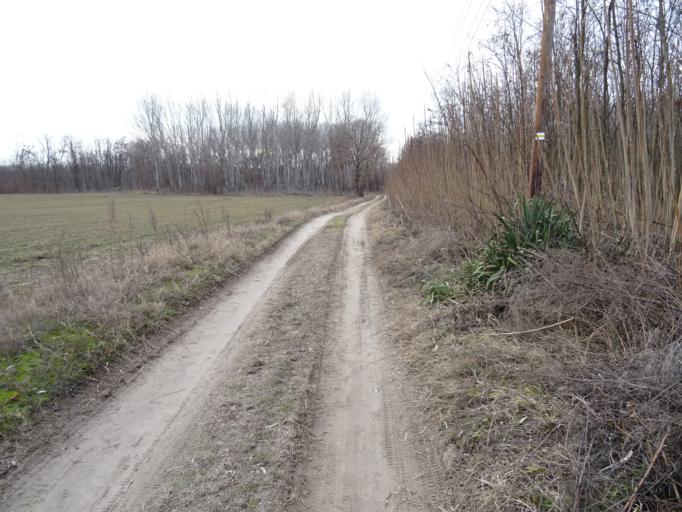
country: HU
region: Bacs-Kiskun
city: Szabadszallas
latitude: 46.8704
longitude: 19.2925
